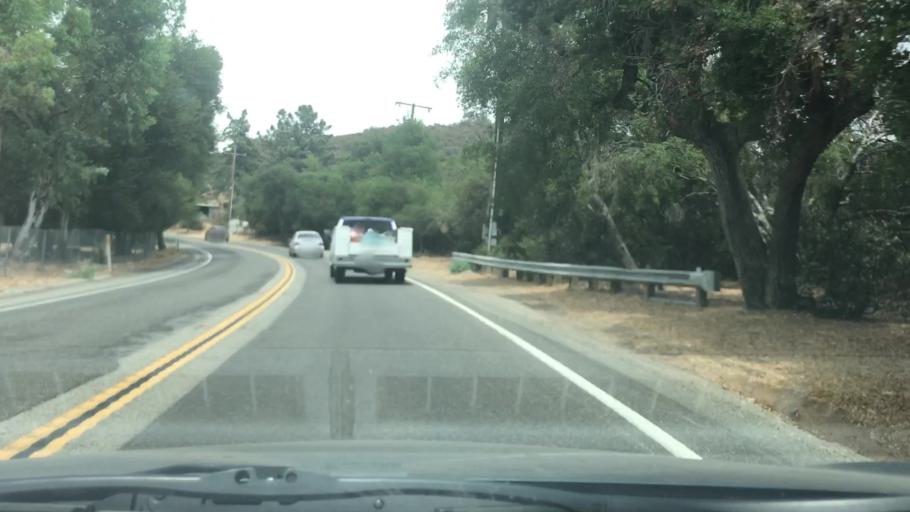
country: US
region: California
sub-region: Riverside County
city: Lakeland Village
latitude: 33.6470
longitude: -117.4171
